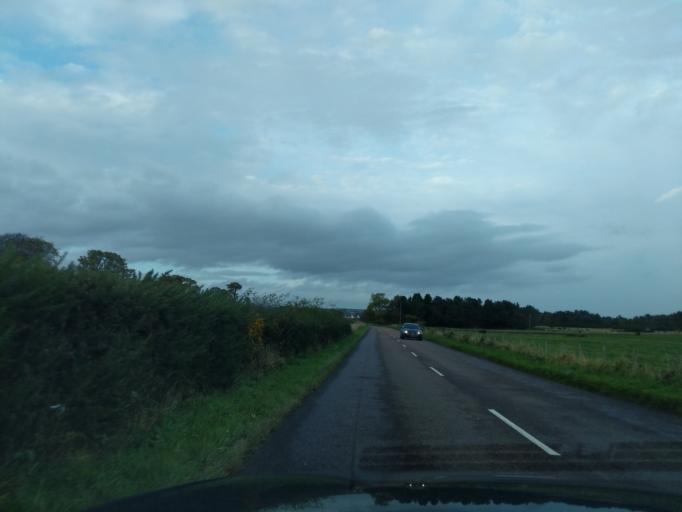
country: GB
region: Scotland
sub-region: Fife
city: Tayport
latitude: 56.4336
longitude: -2.8850
